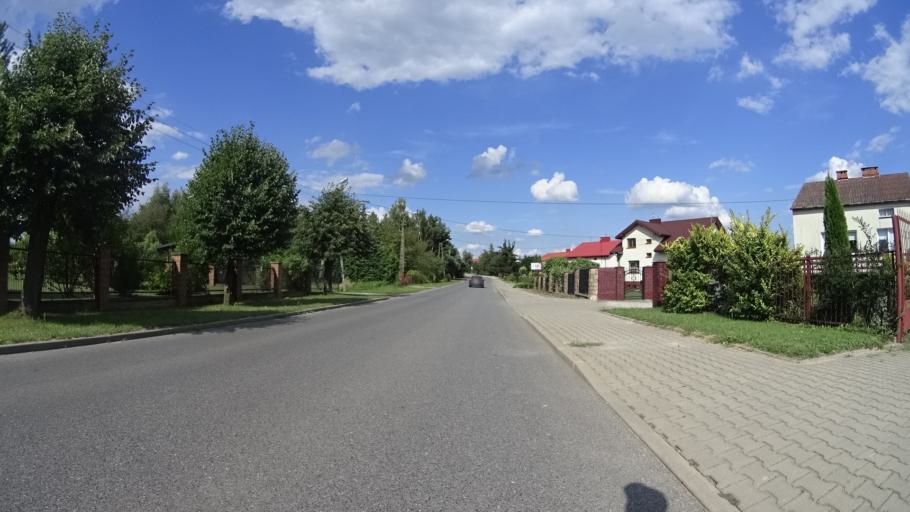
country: PL
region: Masovian Voivodeship
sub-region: Powiat grojecki
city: Mogielnica
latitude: 51.6836
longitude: 20.7161
